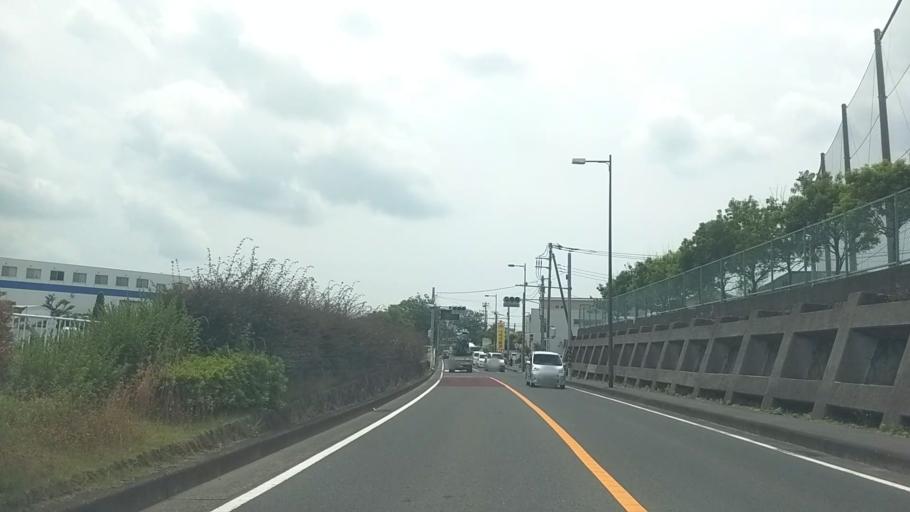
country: JP
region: Kanagawa
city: Fujisawa
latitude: 35.3404
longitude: 139.4671
